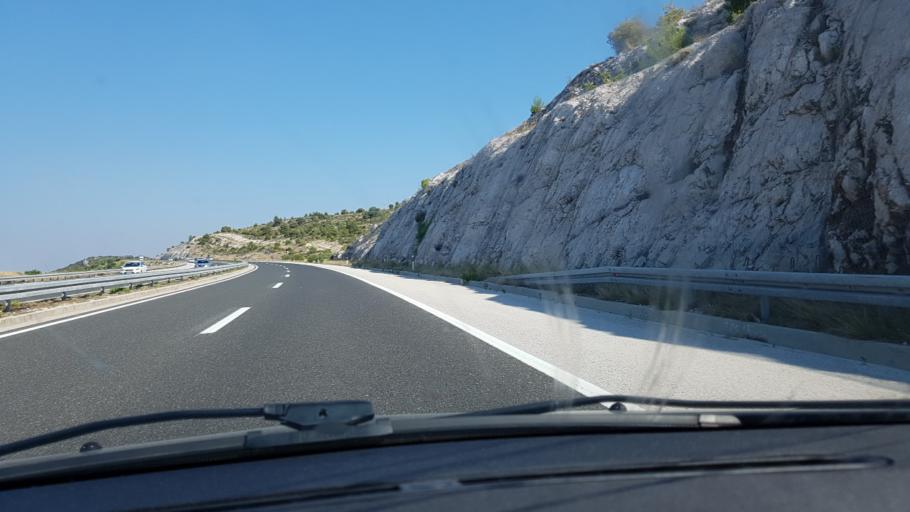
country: HR
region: Sibensko-Kniniska
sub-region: Grad Sibenik
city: Brodarica
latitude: 43.7203
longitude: 15.9855
